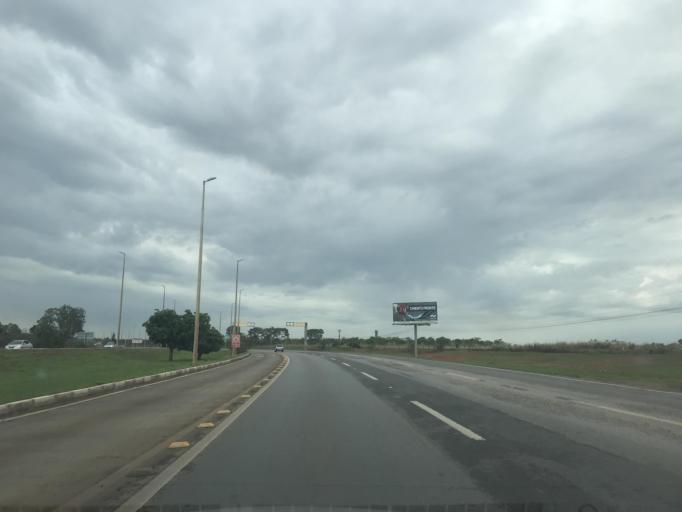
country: BR
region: Federal District
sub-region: Brasilia
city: Brasilia
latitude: -15.9509
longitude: -47.9943
